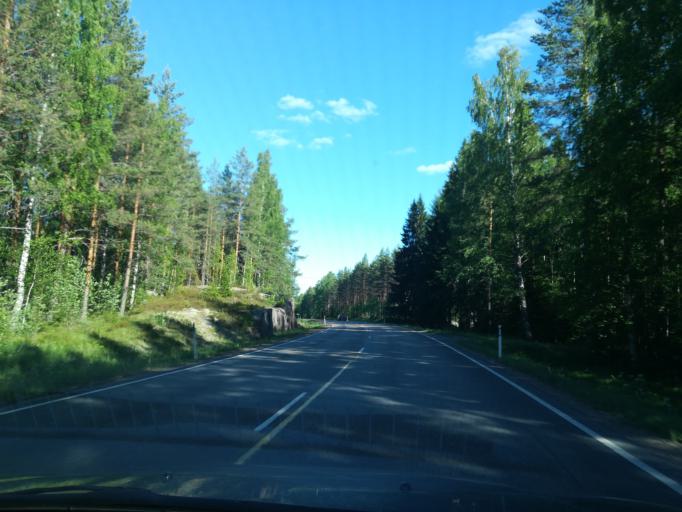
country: FI
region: South Karelia
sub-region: Imatra
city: Ruokolahti
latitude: 61.3668
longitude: 28.6820
